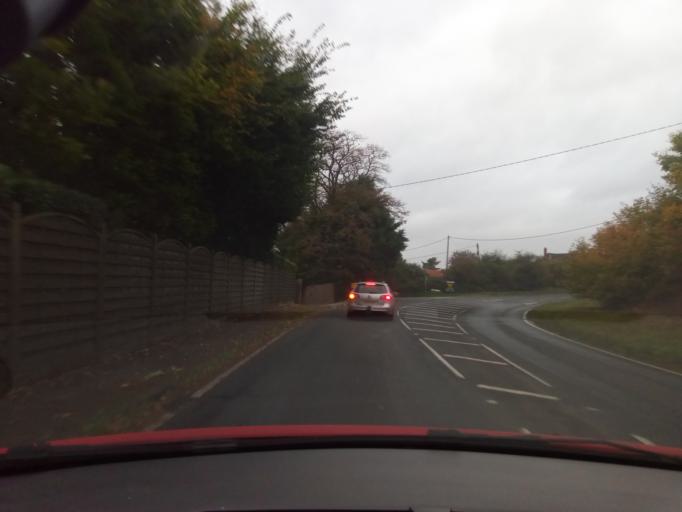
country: GB
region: England
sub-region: Essex
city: Great Yeldham
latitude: 52.0208
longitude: 0.5537
